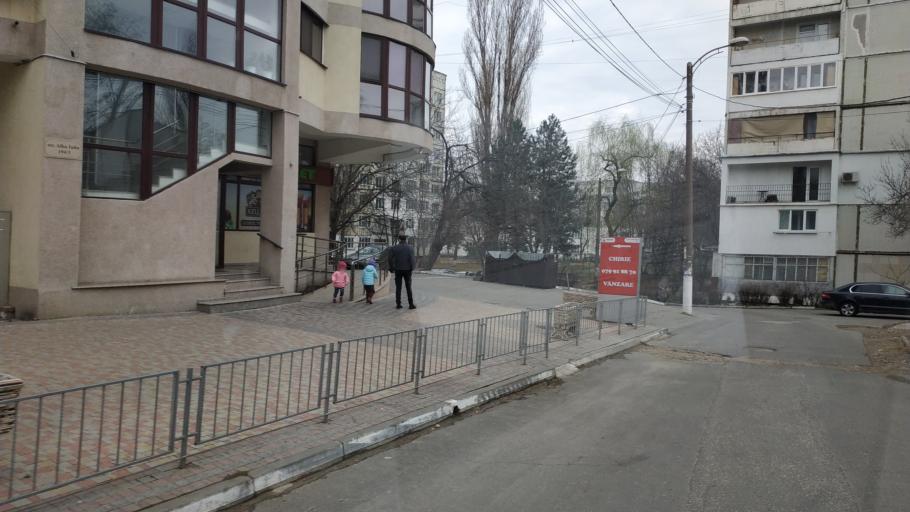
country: MD
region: Chisinau
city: Vatra
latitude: 47.0392
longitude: 28.7722
